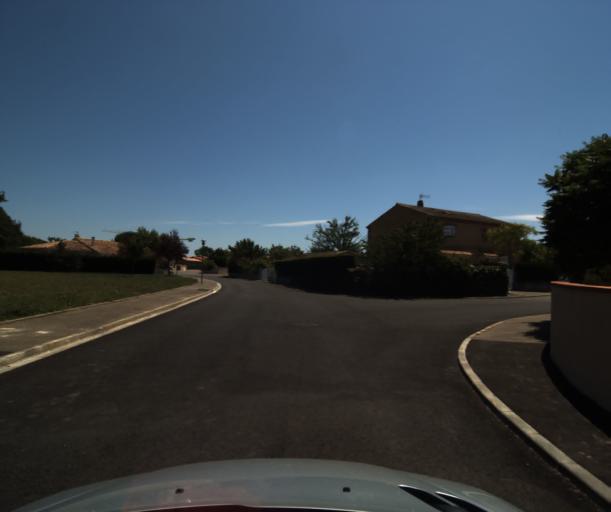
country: FR
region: Midi-Pyrenees
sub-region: Departement de la Haute-Garonne
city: Roquettes
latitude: 43.4965
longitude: 1.3667
